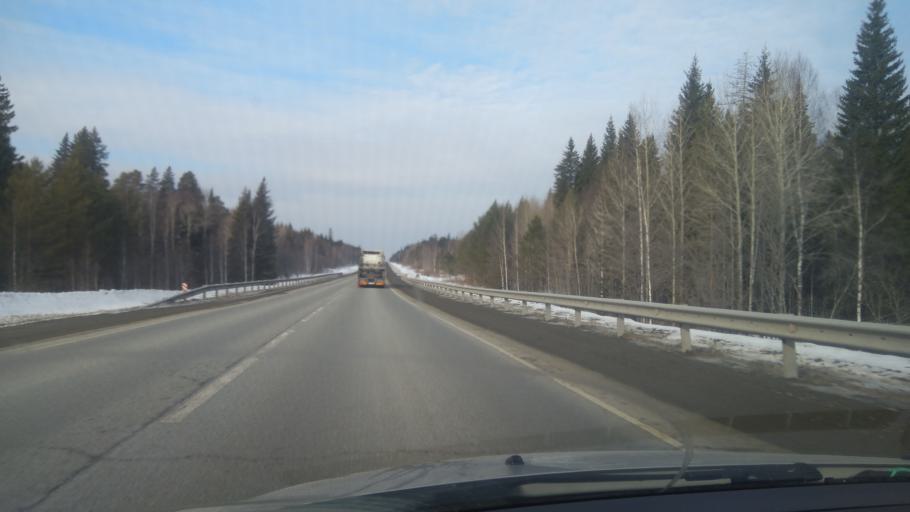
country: RU
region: Sverdlovsk
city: Druzhinino
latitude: 56.7974
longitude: 59.4520
